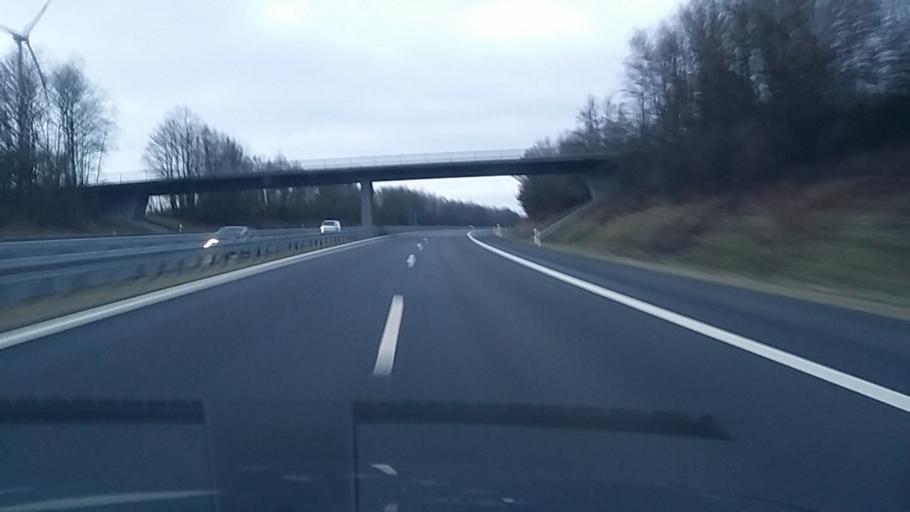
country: DE
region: Bavaria
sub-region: Upper Palatinate
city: Pilsach
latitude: 49.2992
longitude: 11.5514
